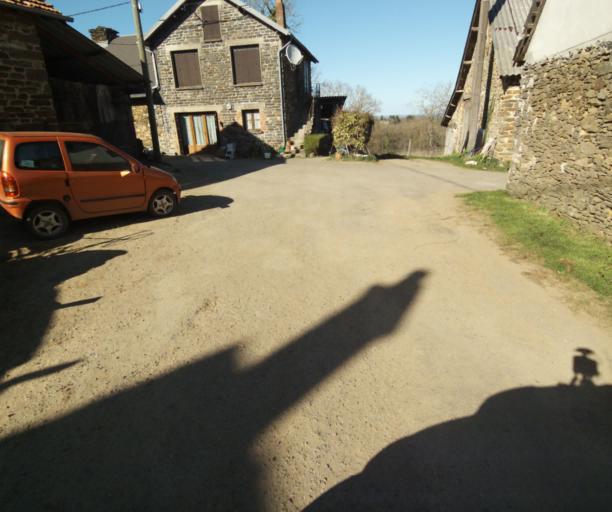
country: FR
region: Limousin
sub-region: Departement de la Correze
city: Chamboulive
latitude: 45.4113
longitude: 1.6556
